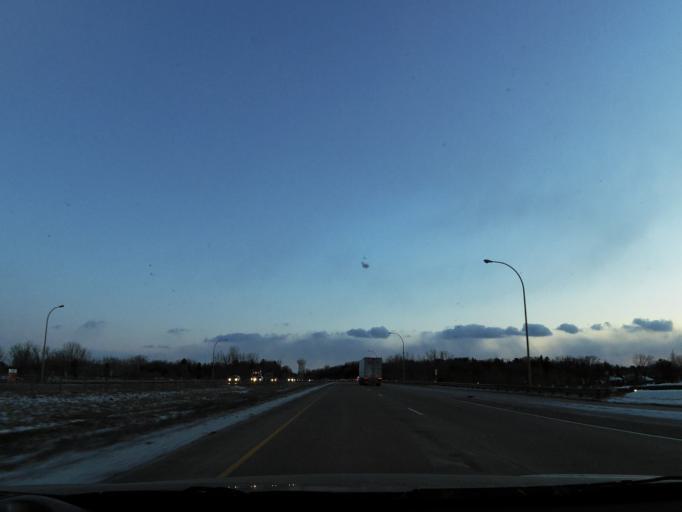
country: US
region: Minnesota
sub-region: Washington County
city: Oakdale
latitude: 44.9954
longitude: -92.9600
